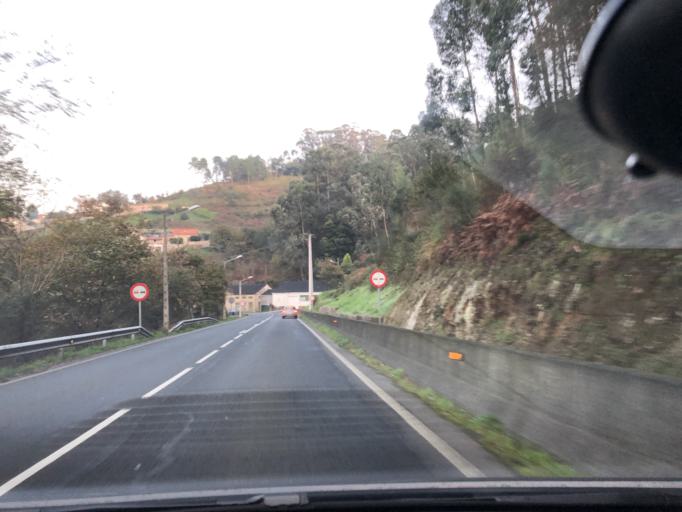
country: ES
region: Galicia
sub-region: Provincia de Pontevedra
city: Marin
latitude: 42.3812
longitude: -8.7184
